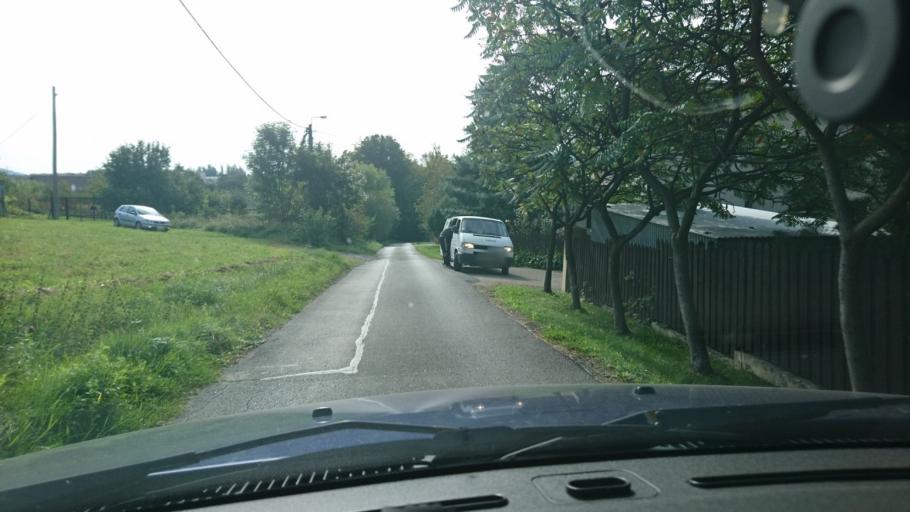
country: PL
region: Silesian Voivodeship
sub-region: Powiat bielski
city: Mazancowice
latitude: 49.8143
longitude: 18.9883
